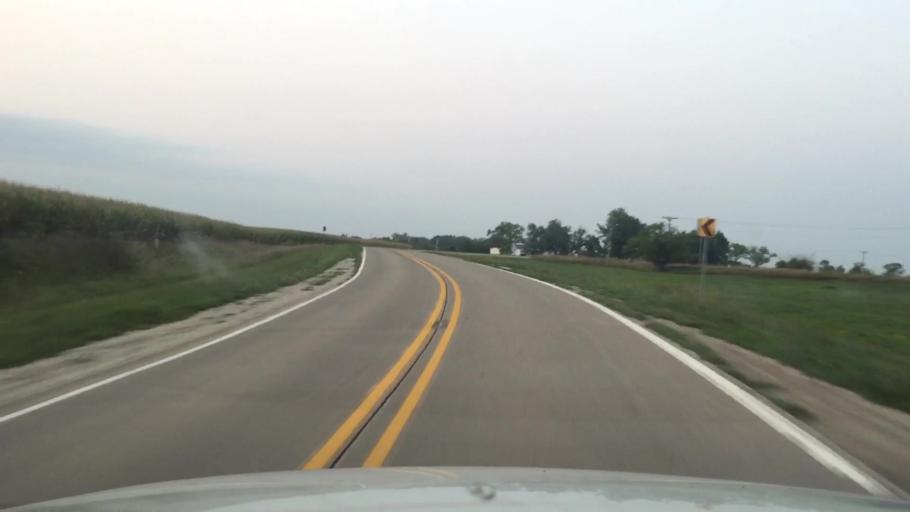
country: US
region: Iowa
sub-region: Clarke County
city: Osceola
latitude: 41.1886
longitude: -93.6743
